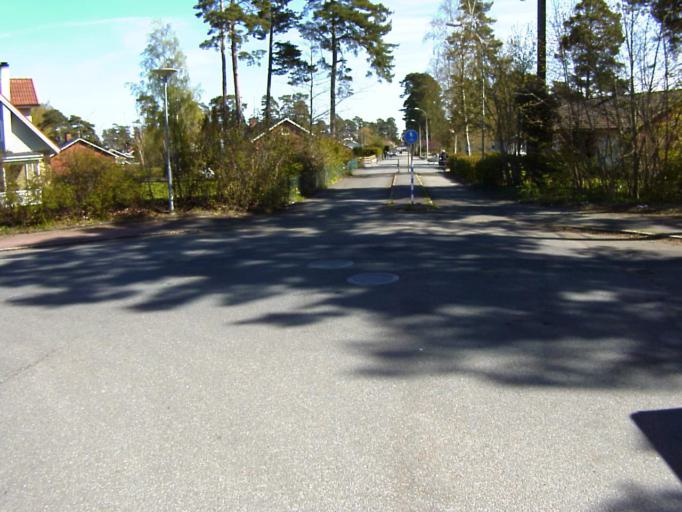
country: SE
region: Skane
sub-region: Kristianstads Kommun
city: Norra Asum
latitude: 55.9999
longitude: 14.0806
